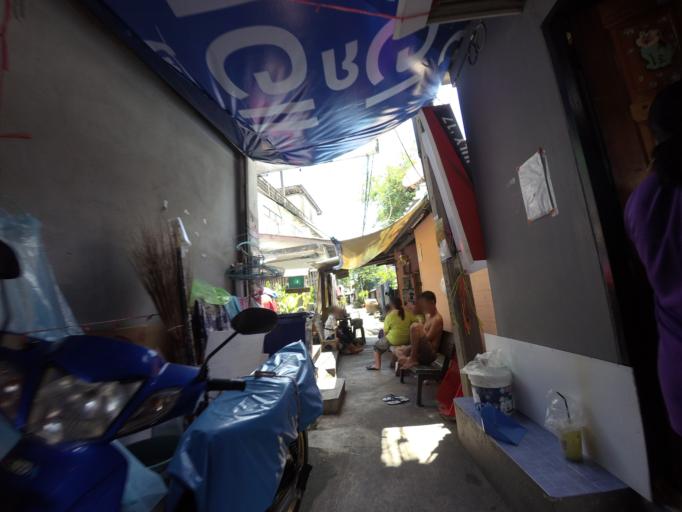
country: TH
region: Bangkok
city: Lat Phrao
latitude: 13.8056
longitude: 100.5884
